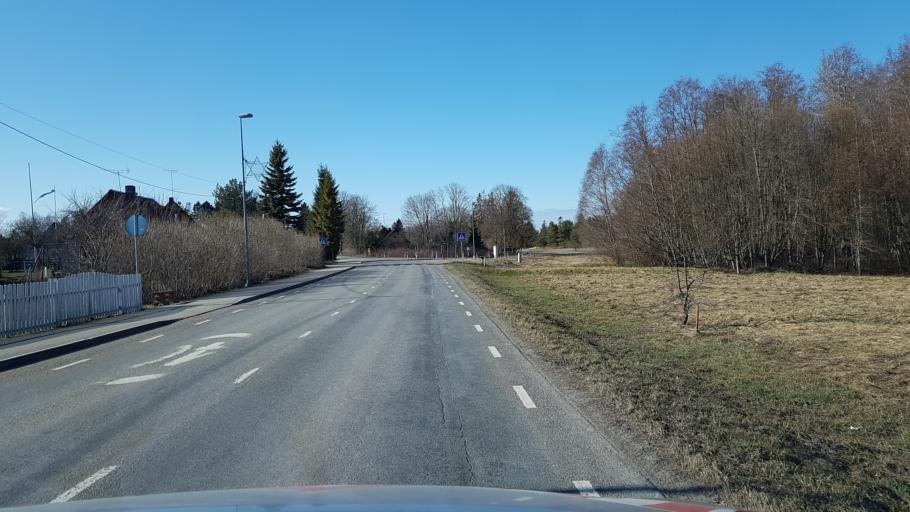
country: EE
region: Laeaene-Virumaa
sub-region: Haljala vald
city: Haljala
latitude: 59.4390
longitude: 26.2621
